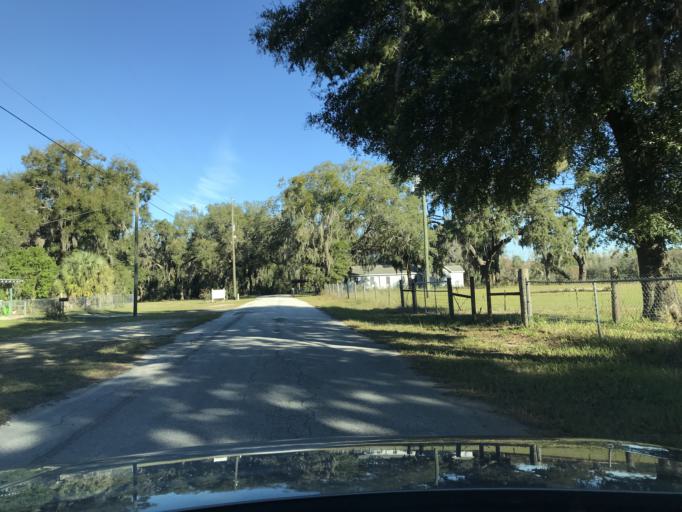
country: US
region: Florida
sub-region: Sumter County
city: Lake Panasoffkee
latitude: 28.7551
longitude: -82.0974
